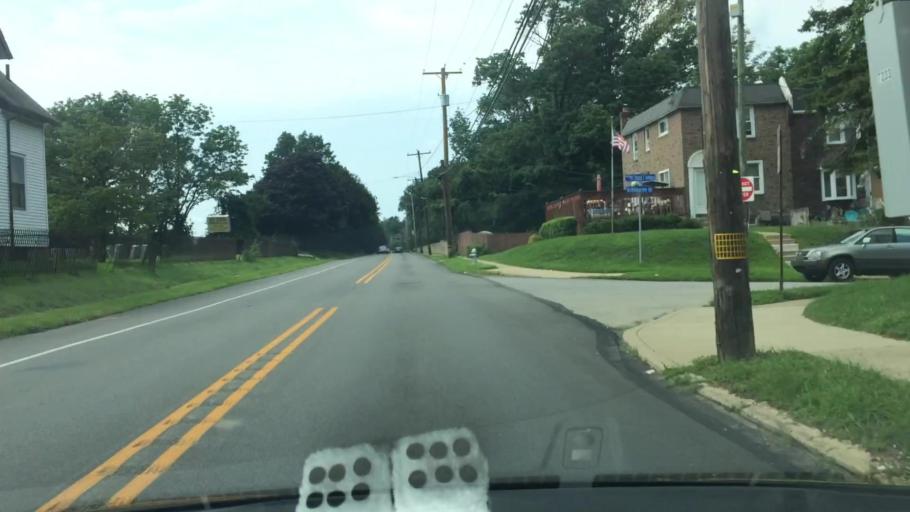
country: US
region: Pennsylvania
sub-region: Delaware County
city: Collingdale
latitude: 39.9201
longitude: -75.2702
